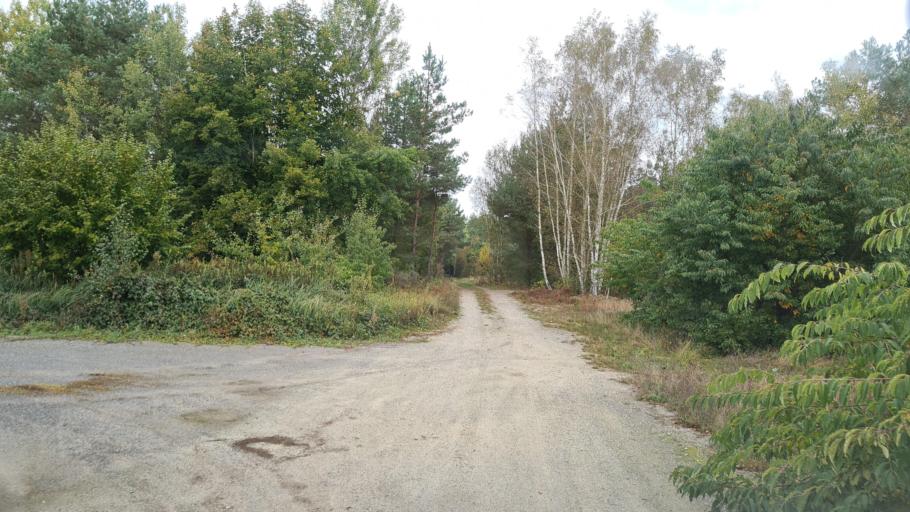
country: DE
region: Brandenburg
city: Altdobern
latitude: 51.6713
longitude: 14.1083
